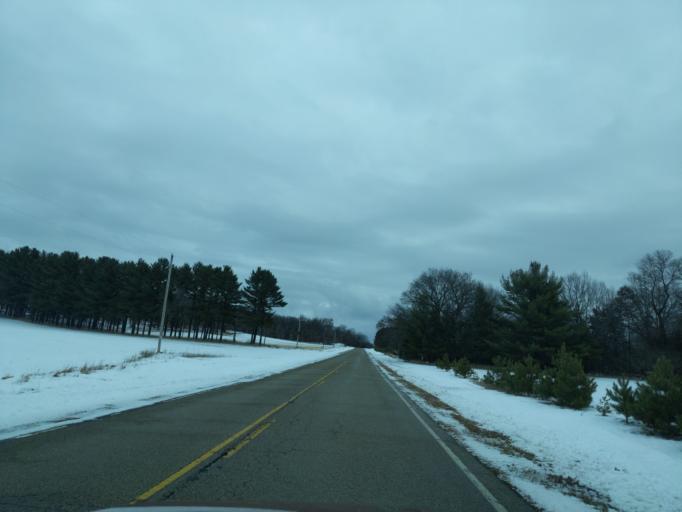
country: US
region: Wisconsin
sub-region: Marquette County
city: Montello
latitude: 43.9136
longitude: -89.3521
